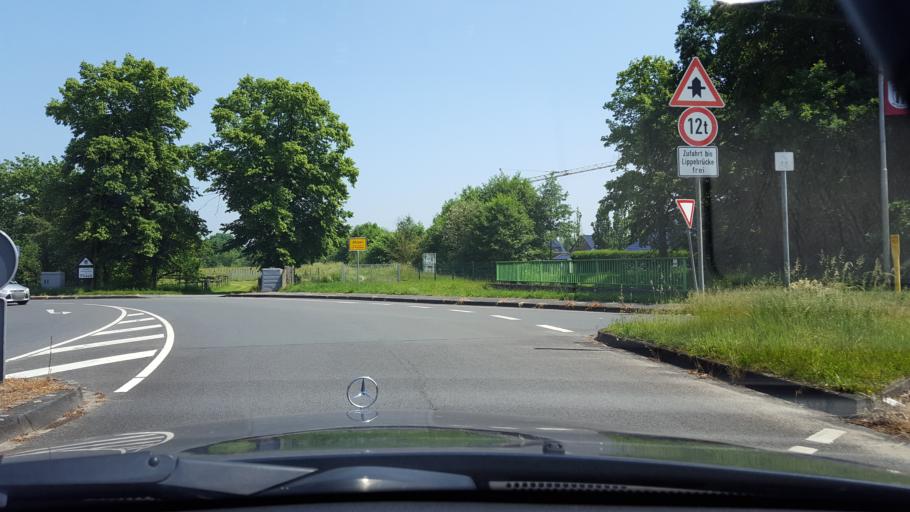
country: DE
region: North Rhine-Westphalia
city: Olfen
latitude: 51.6983
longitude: 7.3088
